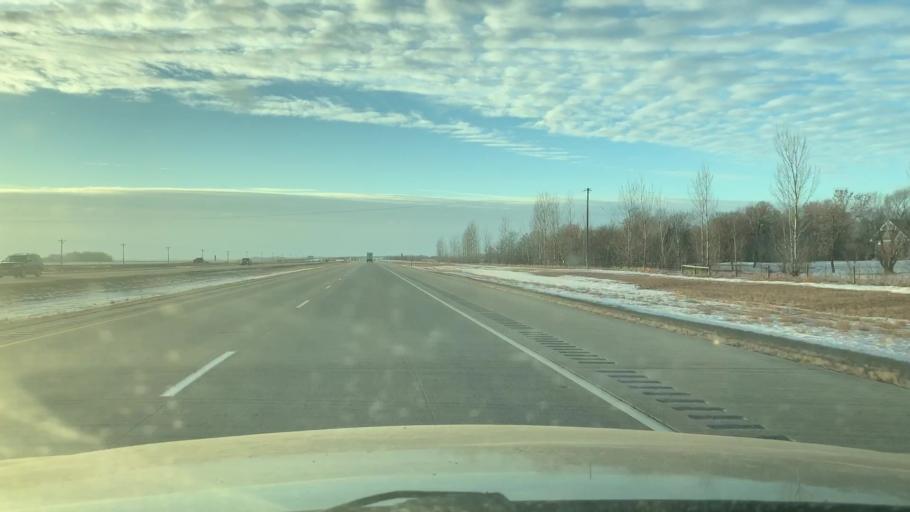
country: US
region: North Dakota
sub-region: Cass County
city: Casselton
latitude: 46.8766
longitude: -97.3180
